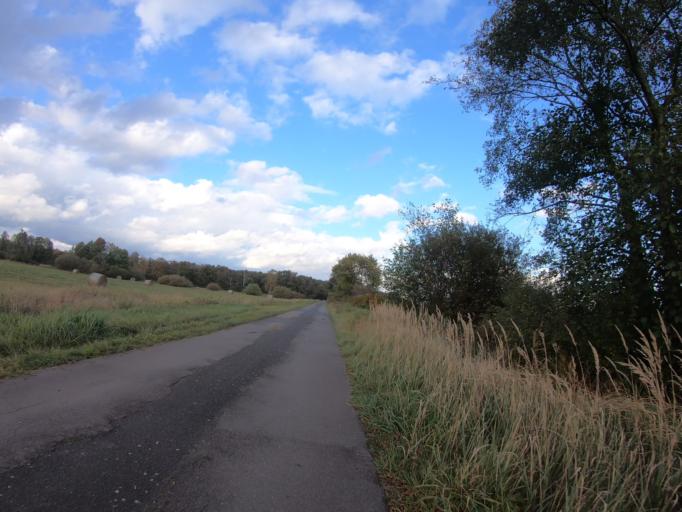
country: DE
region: Lower Saxony
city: Wagenhoff
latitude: 52.5447
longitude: 10.5583
